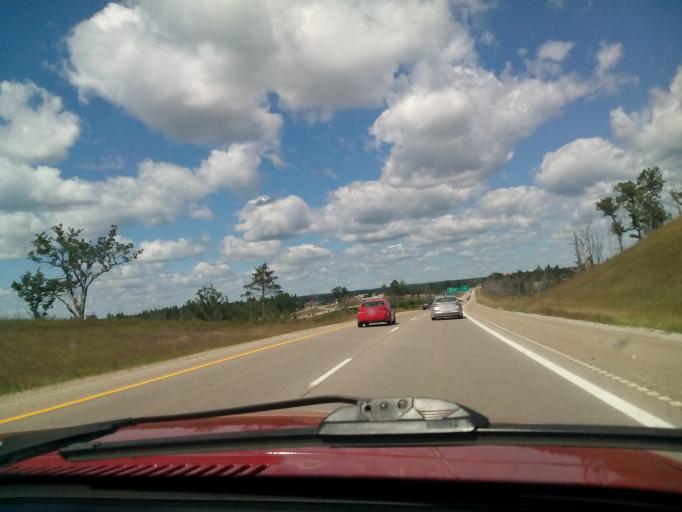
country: US
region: Michigan
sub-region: Crawford County
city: Grayling
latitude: 44.6377
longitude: -84.7078
